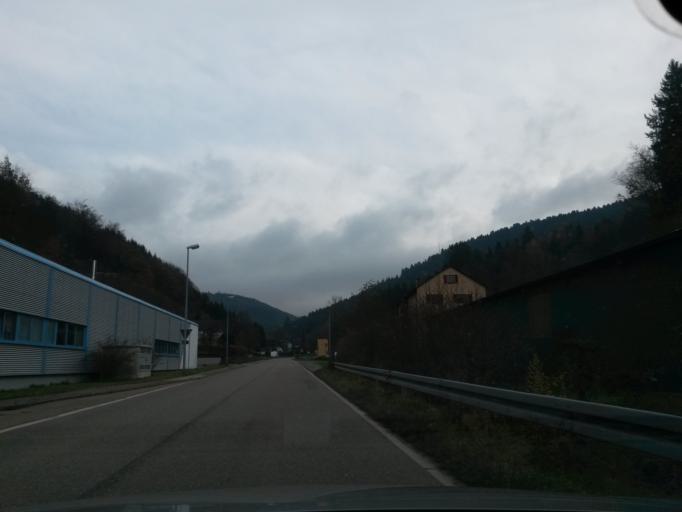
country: DE
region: Baden-Wuerttemberg
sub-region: Karlsruhe Region
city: Alpirsbach
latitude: 48.3476
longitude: 8.4148
